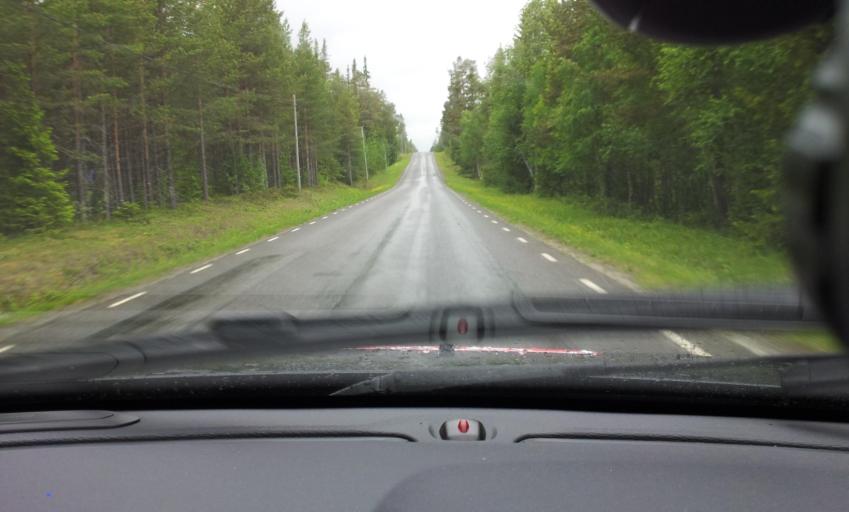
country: SE
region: Jaemtland
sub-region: Are Kommun
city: Are
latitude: 63.1791
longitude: 13.1078
